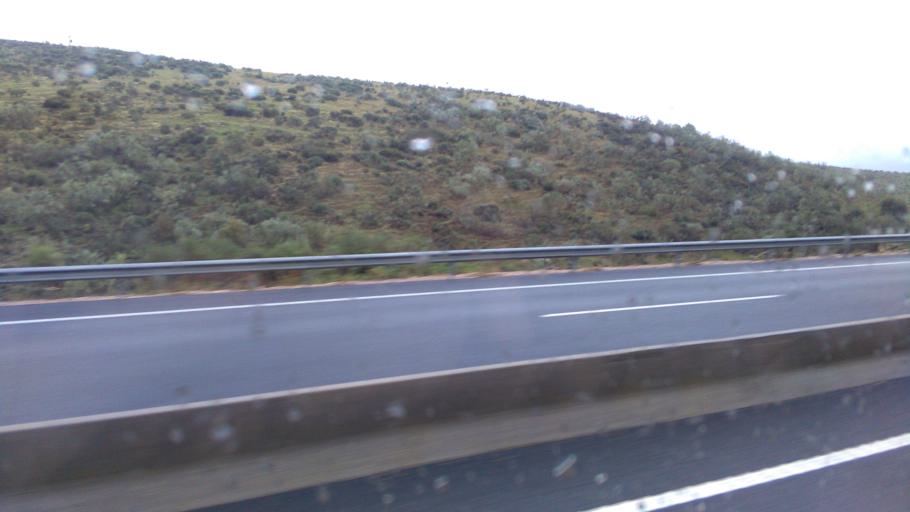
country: ES
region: Extremadura
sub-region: Provincia de Caceres
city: Romangordo
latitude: 39.7493
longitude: -5.7272
